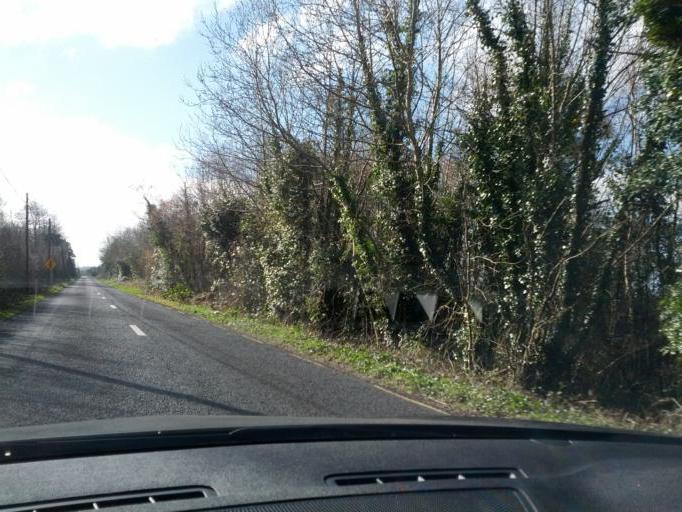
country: IE
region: Connaught
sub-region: County Galway
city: Ballinasloe
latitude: 53.3587
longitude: -8.2570
